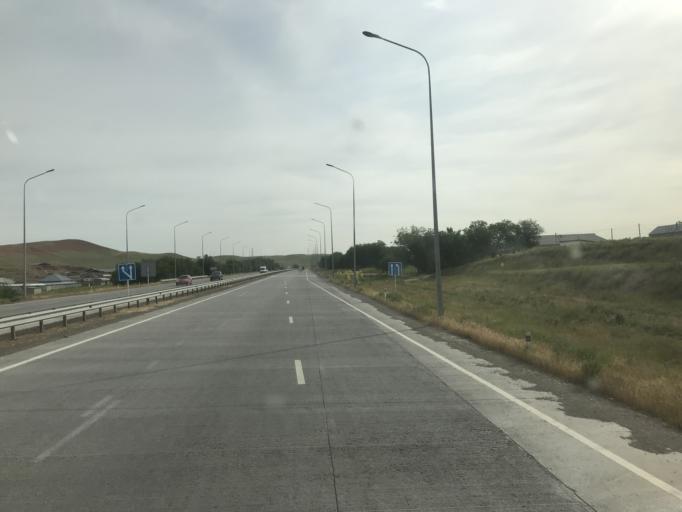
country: KZ
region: Ongtustik Qazaqstan
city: Shymkent
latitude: 42.2141
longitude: 69.5231
